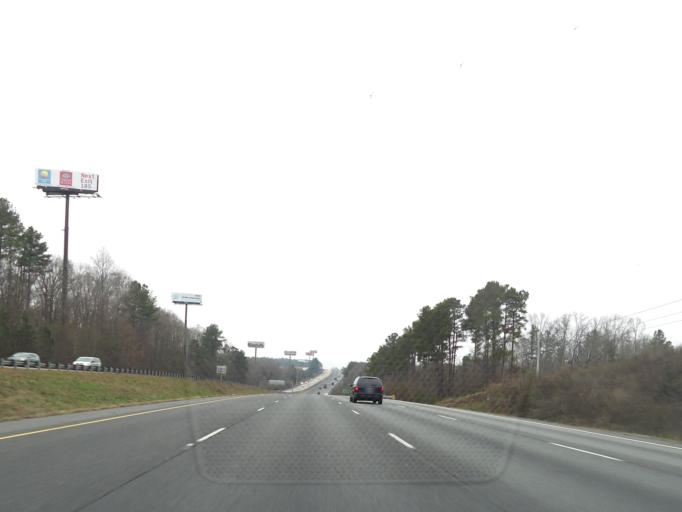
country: US
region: Georgia
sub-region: Monroe County
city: Forsyth
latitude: 32.9958
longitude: -83.8523
